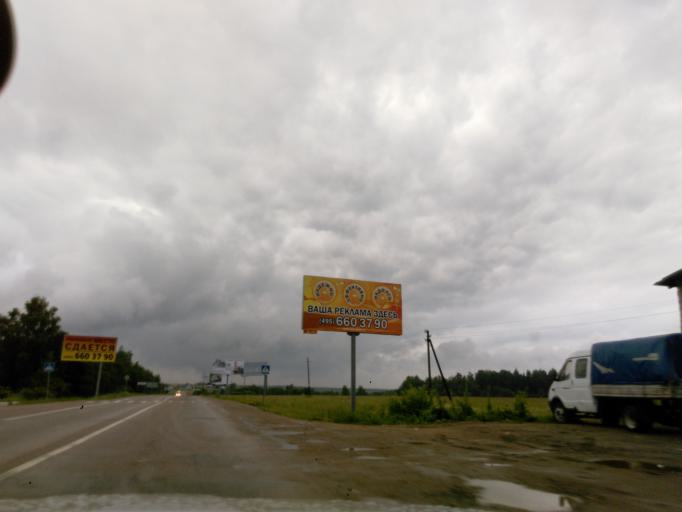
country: RU
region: Moskovskaya
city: Andreyevka
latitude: 55.9710
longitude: 37.0975
